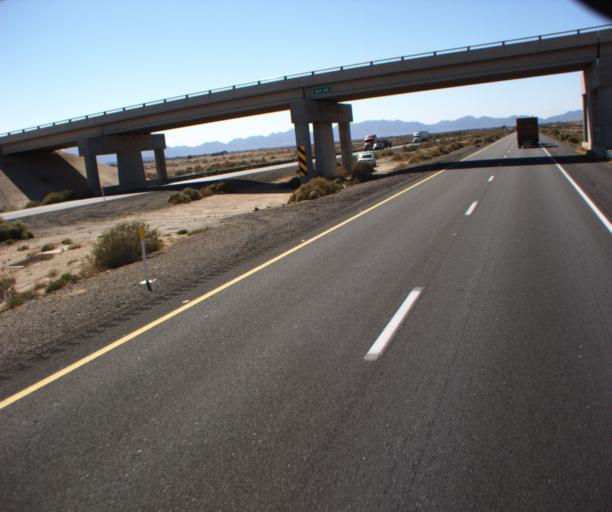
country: US
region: Arizona
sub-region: Yuma County
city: Wellton
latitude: 32.6746
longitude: -114.0730
